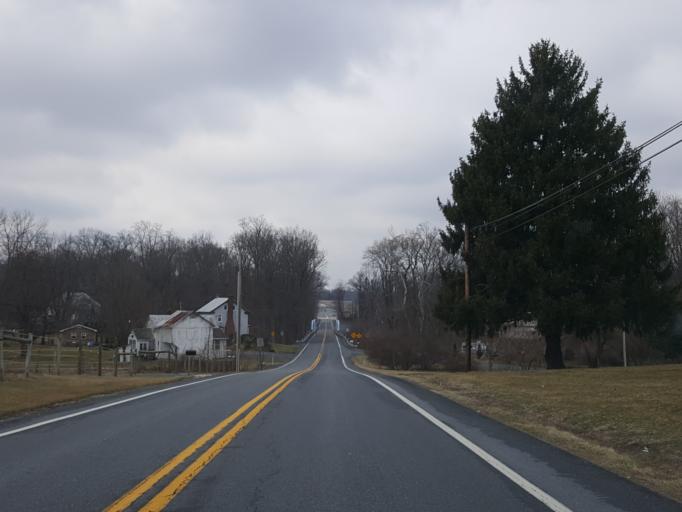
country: US
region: Pennsylvania
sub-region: Lebanon County
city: Jonestown
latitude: 40.4534
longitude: -76.5050
